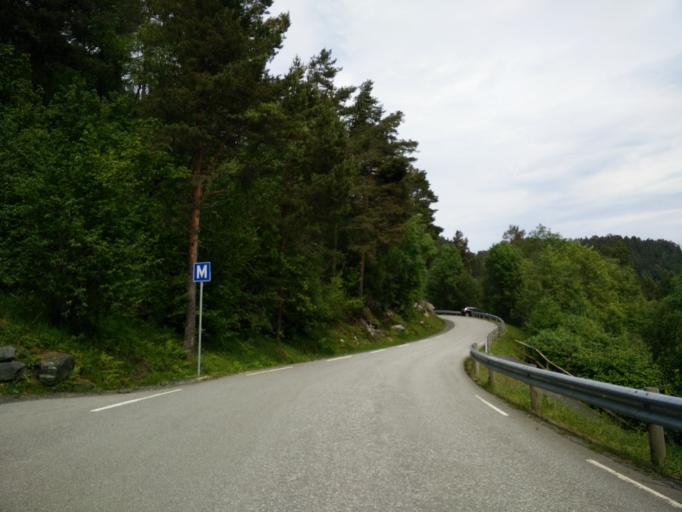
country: NO
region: More og Romsdal
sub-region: Kristiansund
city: Rensvik
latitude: 63.0249
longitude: 7.9529
